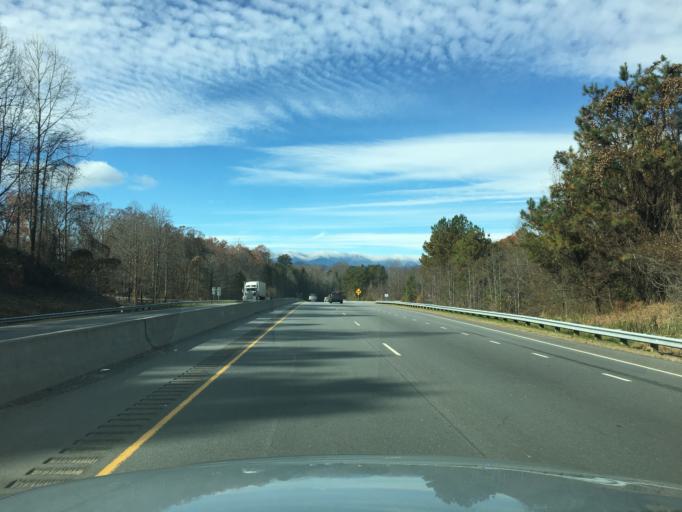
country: US
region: North Carolina
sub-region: McDowell County
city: Marion
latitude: 35.6773
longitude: -82.0234
